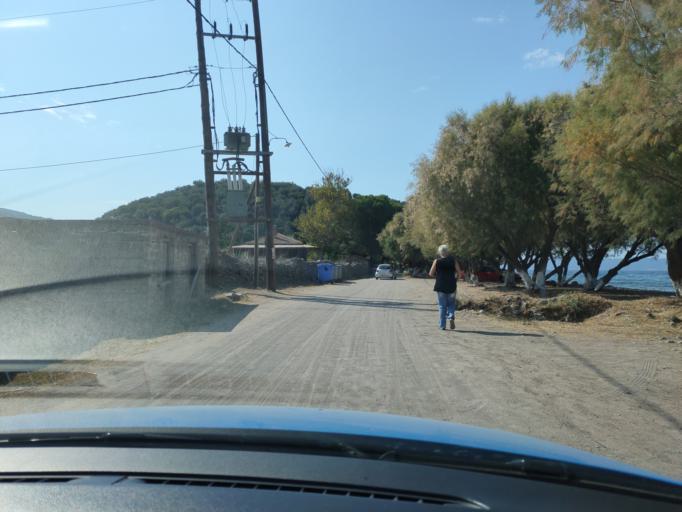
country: GR
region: North Aegean
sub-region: Nomos Lesvou
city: Mantamados
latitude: 39.3741
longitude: 26.3116
